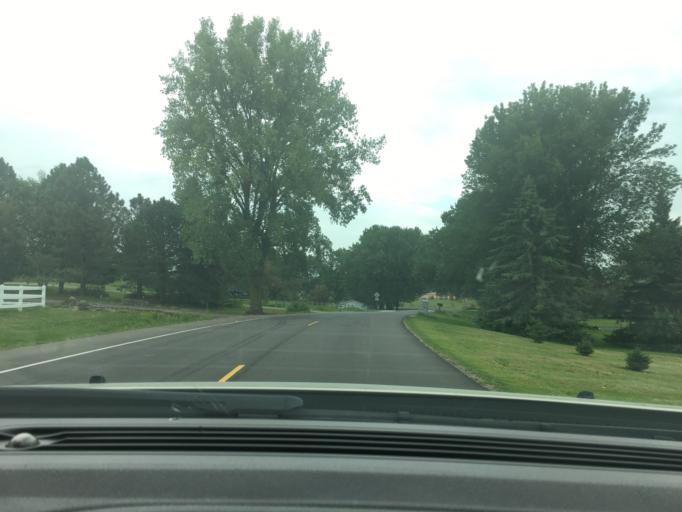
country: US
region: Minnesota
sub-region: Olmsted County
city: Rochester
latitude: 44.0826
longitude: -92.5185
